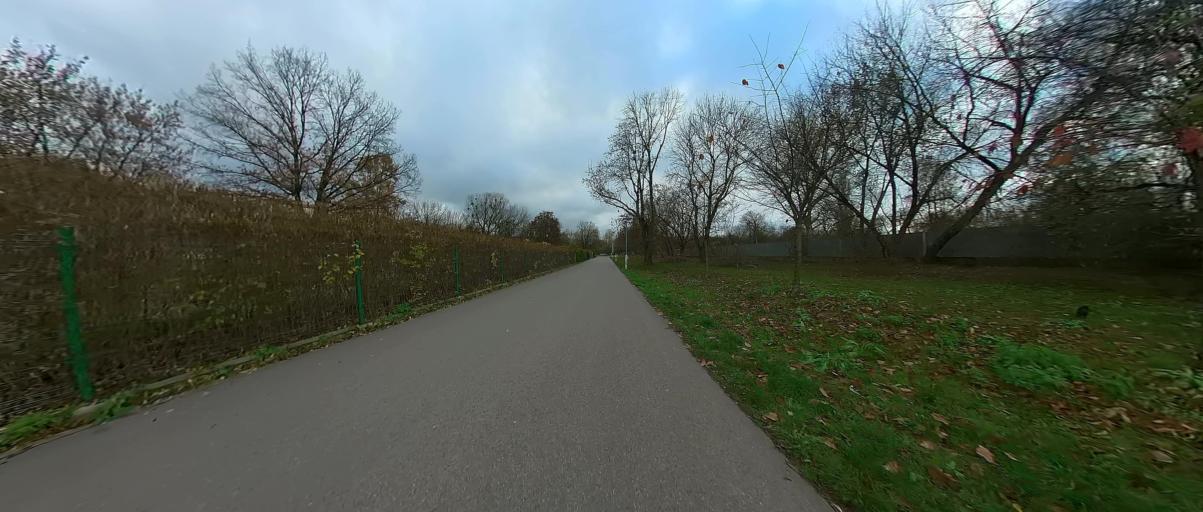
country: PL
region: Masovian Voivodeship
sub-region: Warszawa
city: Ochota
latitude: 52.2140
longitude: 20.9961
